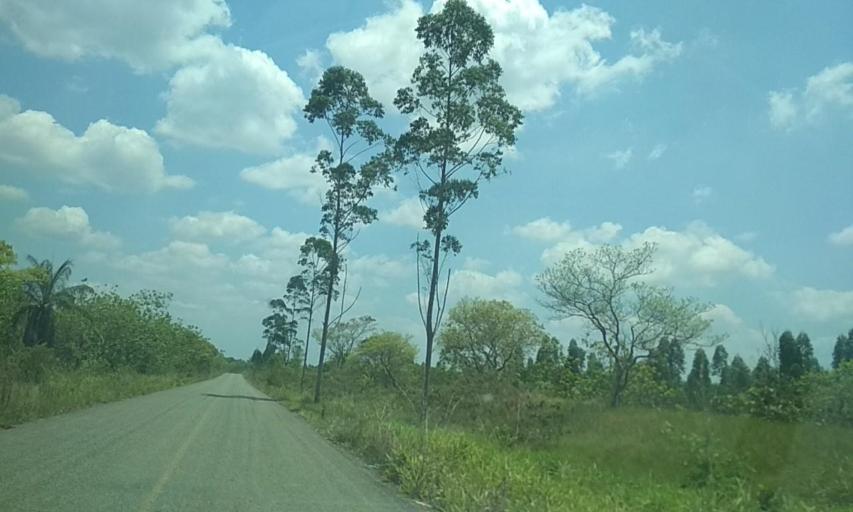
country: MX
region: Tabasco
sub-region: Huimanguillo
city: Francisco Rueda
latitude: 17.7827
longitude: -93.8283
